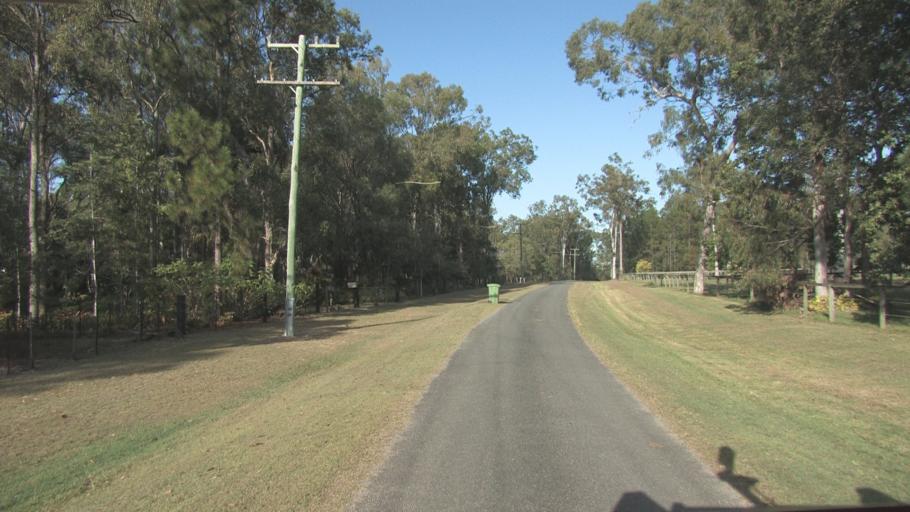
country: AU
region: Queensland
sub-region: Logan
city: Park Ridge South
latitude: -27.7457
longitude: 153.0450
